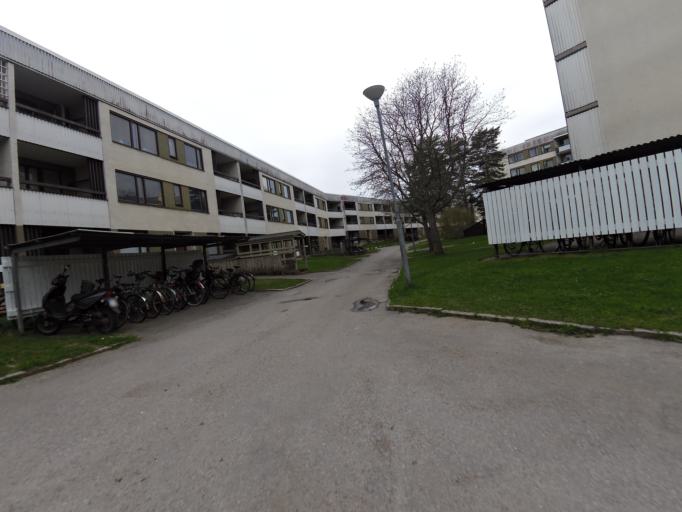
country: SE
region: Gaevleborg
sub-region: Gavle Kommun
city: Gavle
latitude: 60.6917
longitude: 17.1219
